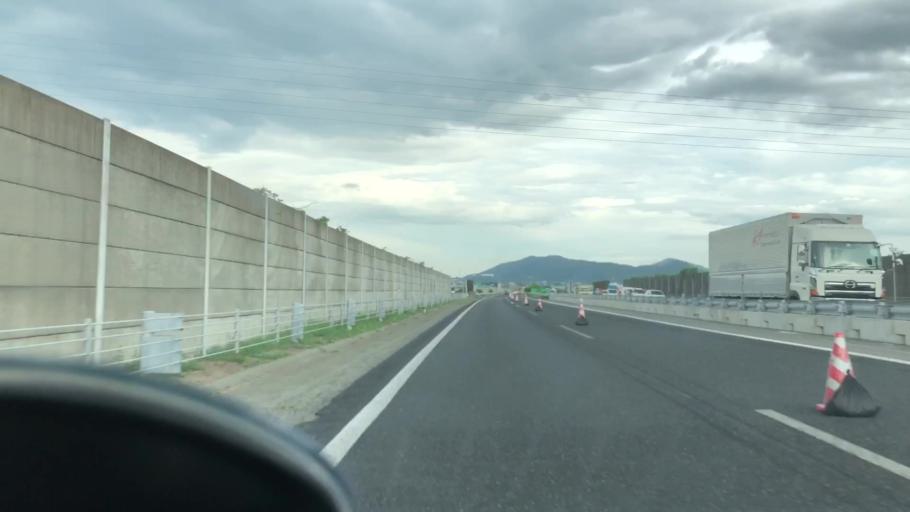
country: JP
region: Hyogo
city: Himeji
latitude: 34.9532
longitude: 134.7427
